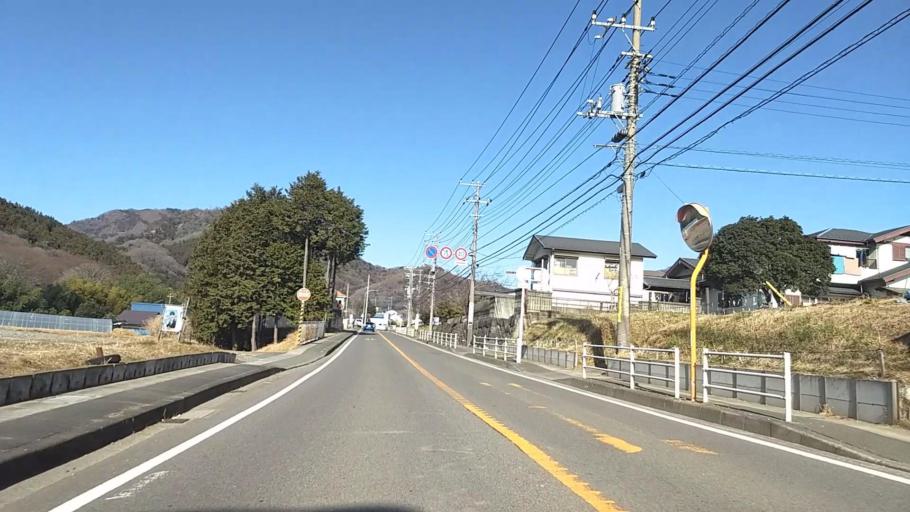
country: JP
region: Kanagawa
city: Atsugi
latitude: 35.4768
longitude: 139.3081
